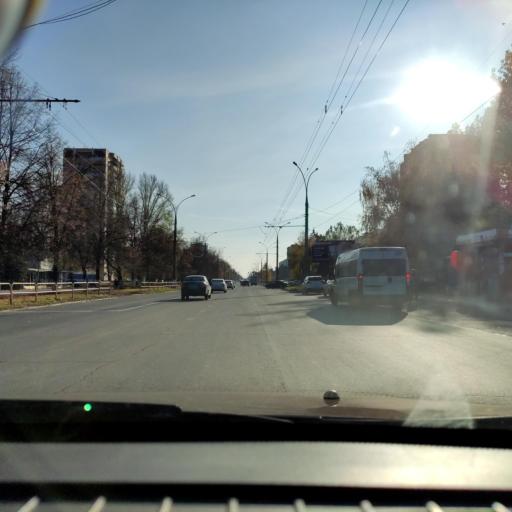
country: RU
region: Samara
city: Tol'yatti
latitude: 53.5338
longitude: 49.2774
